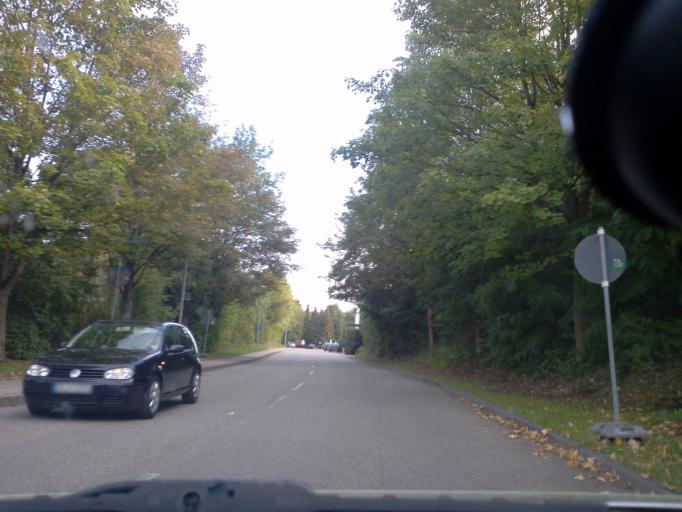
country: DE
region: Baden-Wuerttemberg
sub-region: Regierungsbezirk Stuttgart
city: Gemmingen
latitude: 49.1532
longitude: 8.9793
